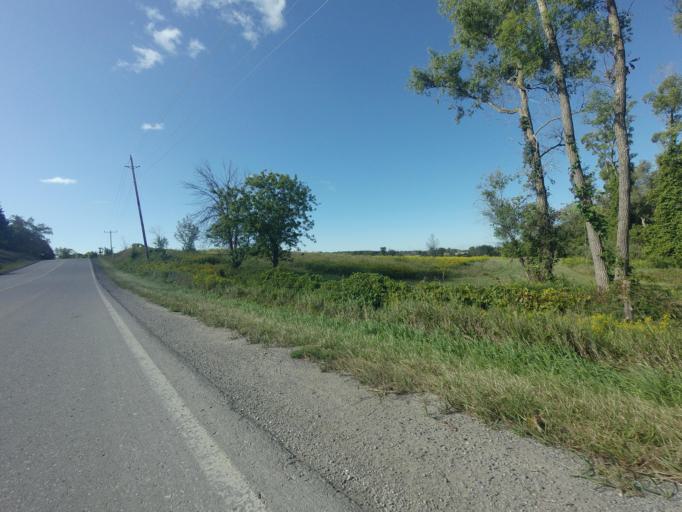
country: CA
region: Ontario
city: Newmarket
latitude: 44.0418
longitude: -79.5561
